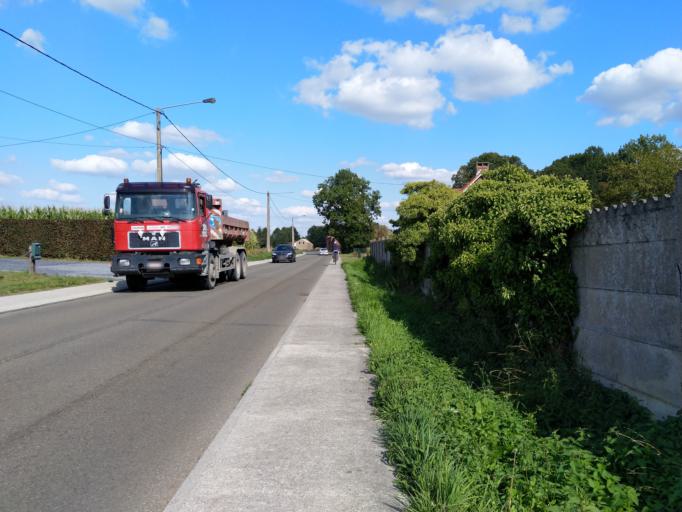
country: BE
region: Wallonia
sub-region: Province du Hainaut
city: Jurbise
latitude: 50.5298
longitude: 3.8686
